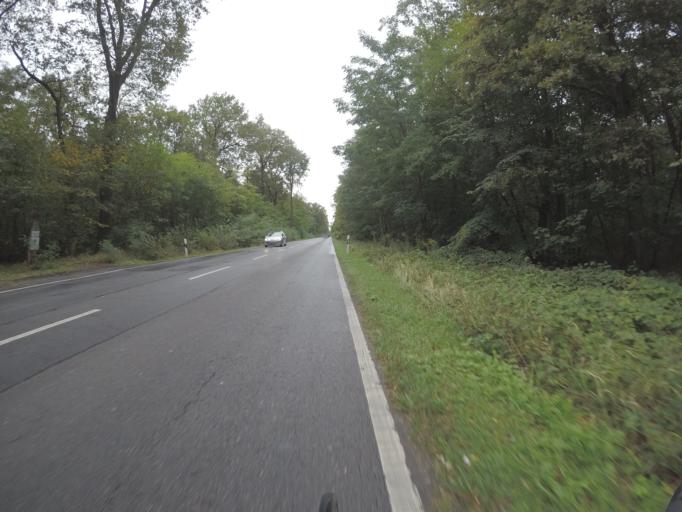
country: DE
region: Berlin
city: Buch
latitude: 52.6350
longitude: 13.4696
